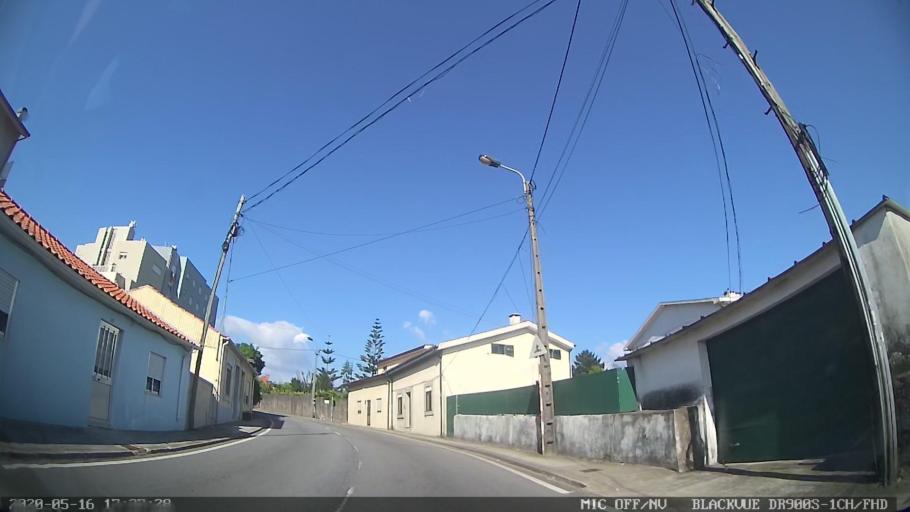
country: PT
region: Porto
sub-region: Gondomar
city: Fanzeres
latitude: 41.1817
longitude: -8.5306
